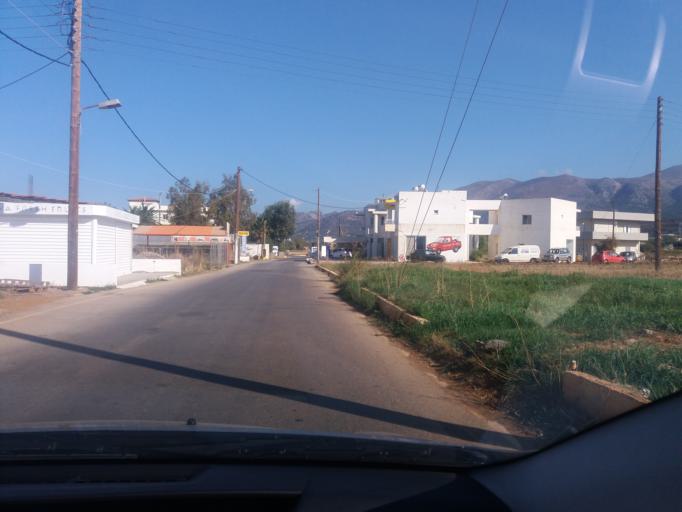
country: GR
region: Crete
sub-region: Nomos Irakleiou
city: Malia
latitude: 35.2924
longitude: 25.4765
